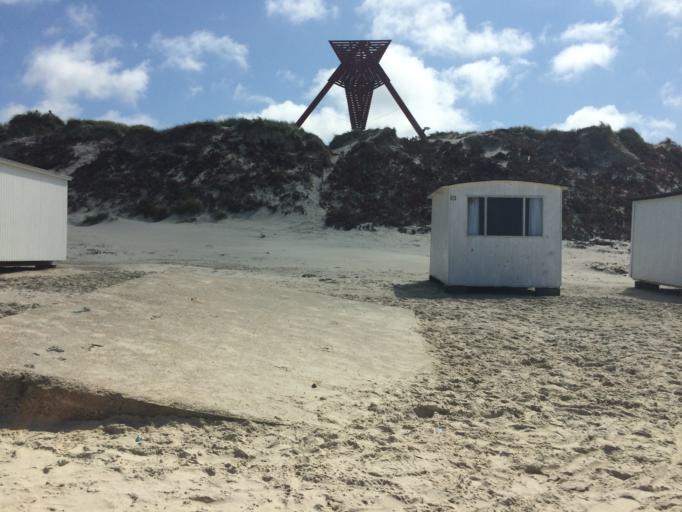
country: DK
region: North Denmark
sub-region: Jammerbugt Kommune
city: Pandrup
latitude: 57.2540
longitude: 9.5782
